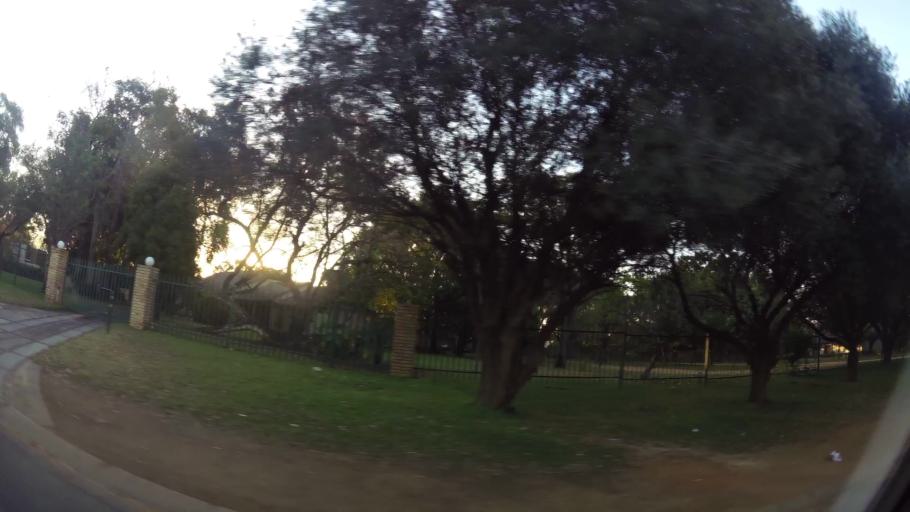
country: ZA
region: North-West
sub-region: Bojanala Platinum District Municipality
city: Rustenburg
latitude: -25.6776
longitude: 27.2199
